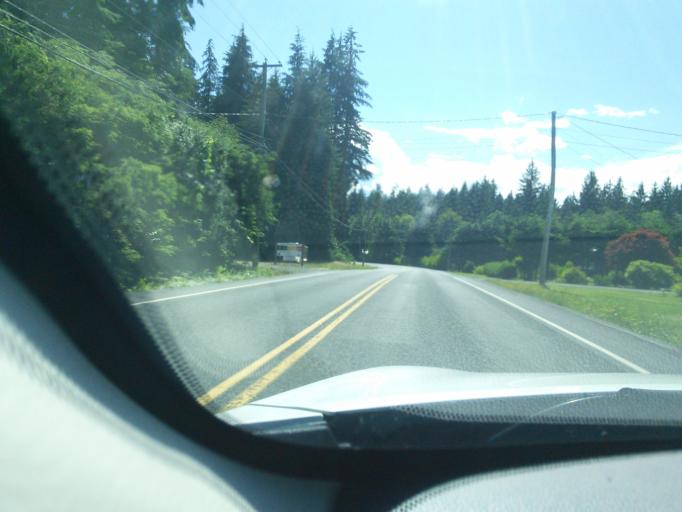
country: CA
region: British Columbia
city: Campbell River
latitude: 50.3335
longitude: -125.9181
